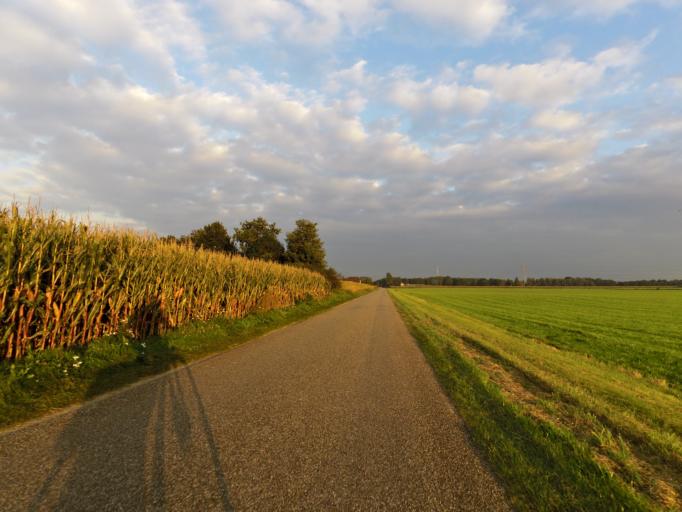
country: NL
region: Gelderland
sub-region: Gemeente Doesburg
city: Doesburg
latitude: 51.9418
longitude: 6.1719
